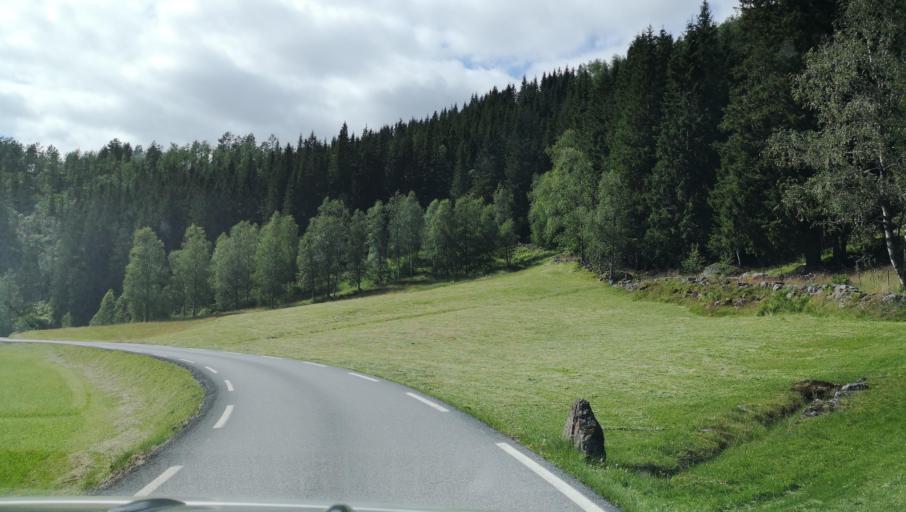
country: NO
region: Hordaland
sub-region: Modalen
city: Mo
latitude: 60.7847
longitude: 5.9515
